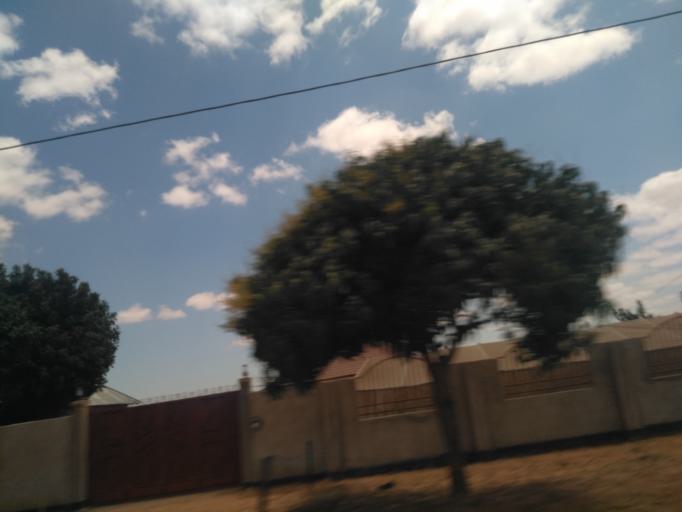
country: TZ
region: Dodoma
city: Kisasa
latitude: -6.1776
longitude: 35.7894
